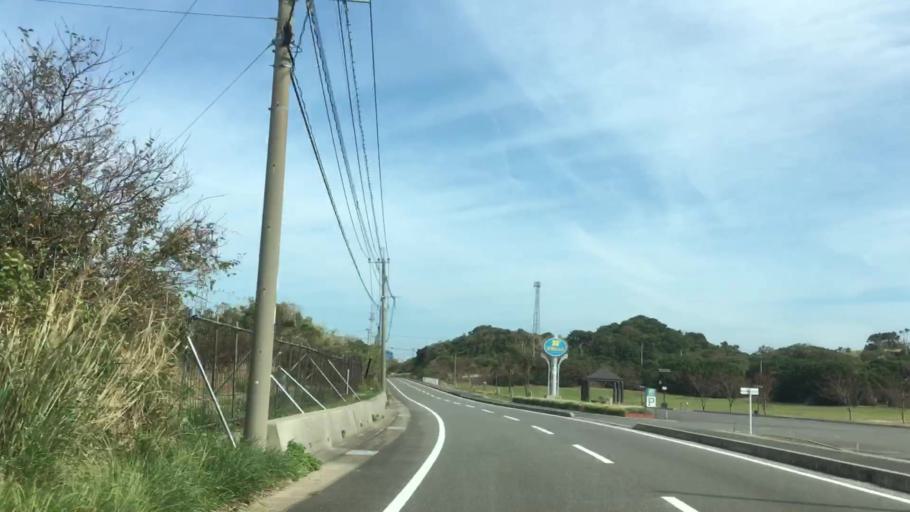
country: JP
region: Nagasaki
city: Sasebo
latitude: 33.0156
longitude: 129.5735
